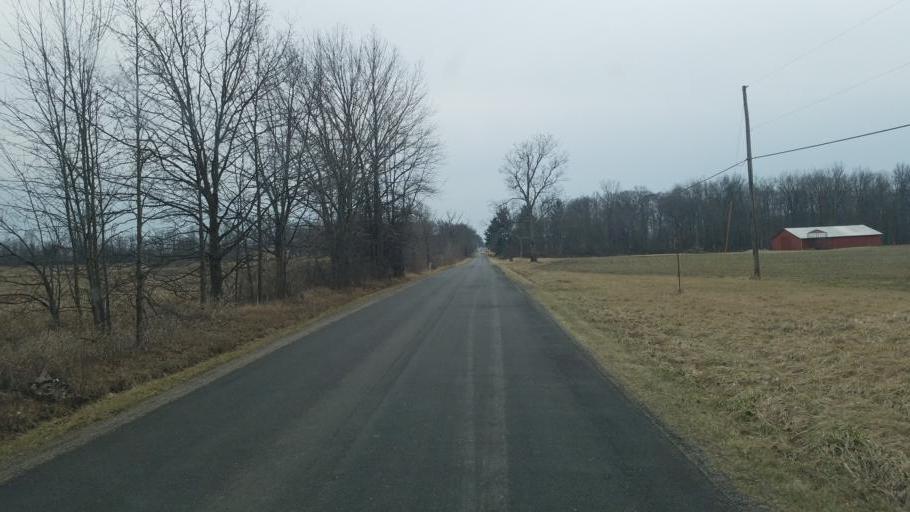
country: US
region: Ohio
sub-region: Crawford County
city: Galion
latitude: 40.6878
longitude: -82.7935
